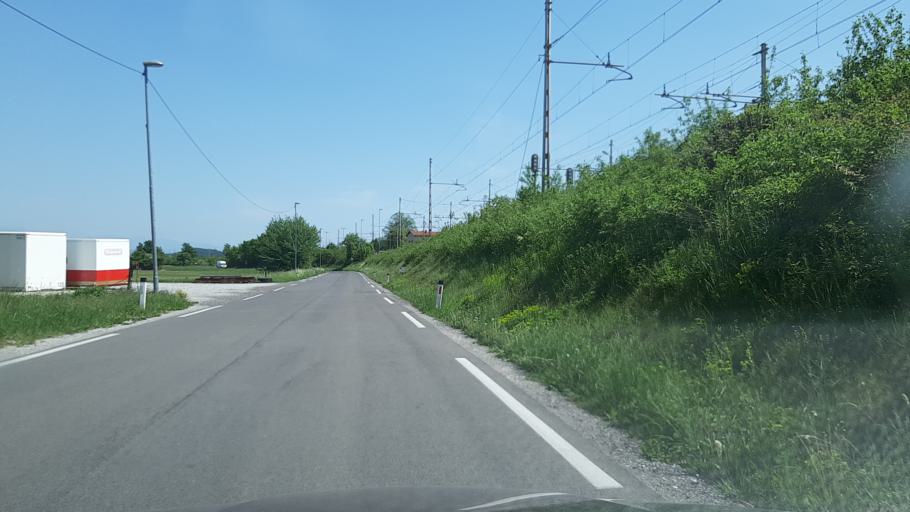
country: SI
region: Brezovica
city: Notranje Gorice
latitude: 45.9640
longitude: 14.3938
